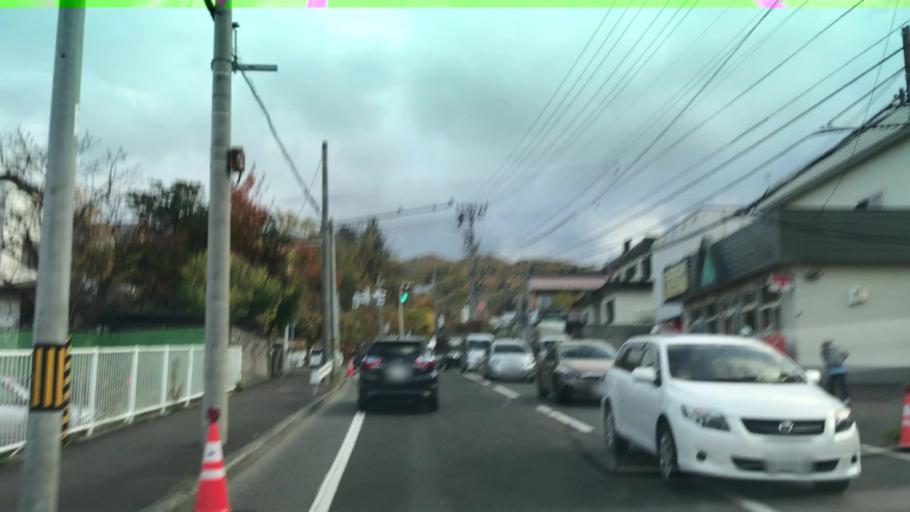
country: JP
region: Hokkaido
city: Sapporo
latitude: 43.0441
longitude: 141.3060
